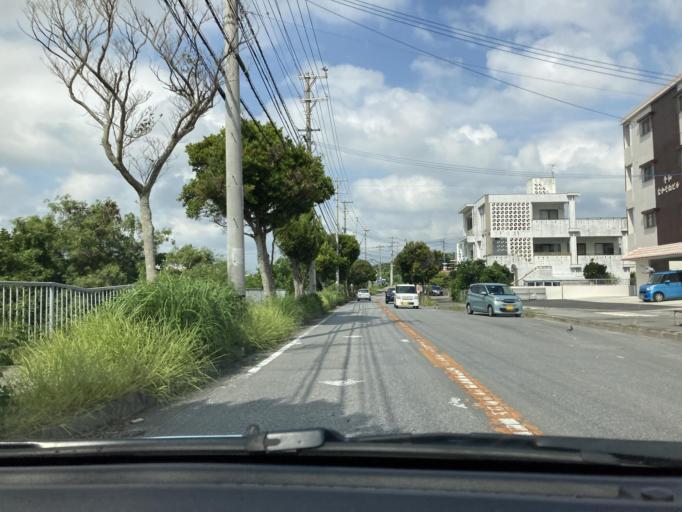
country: JP
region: Okinawa
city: Ginowan
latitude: 26.2331
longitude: 127.7412
